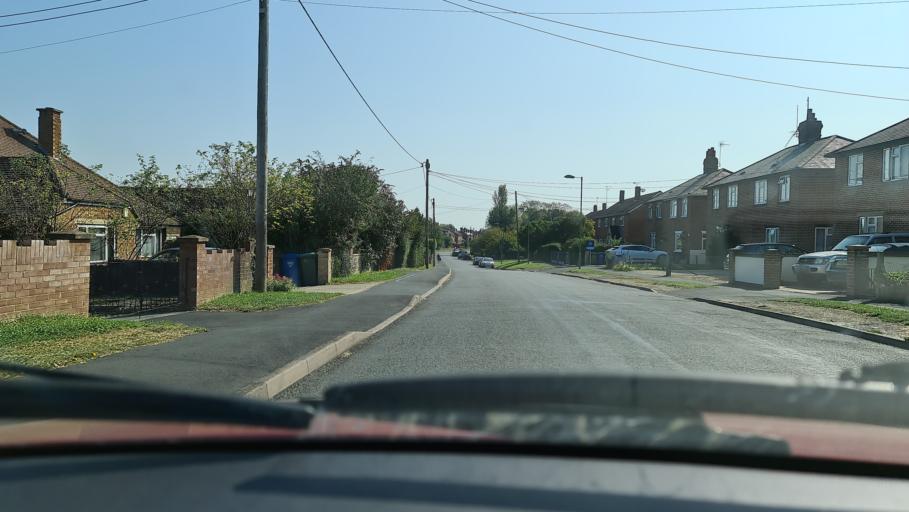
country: GB
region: England
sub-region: Oxfordshire
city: Bicester
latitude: 51.9043
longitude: -1.1598
